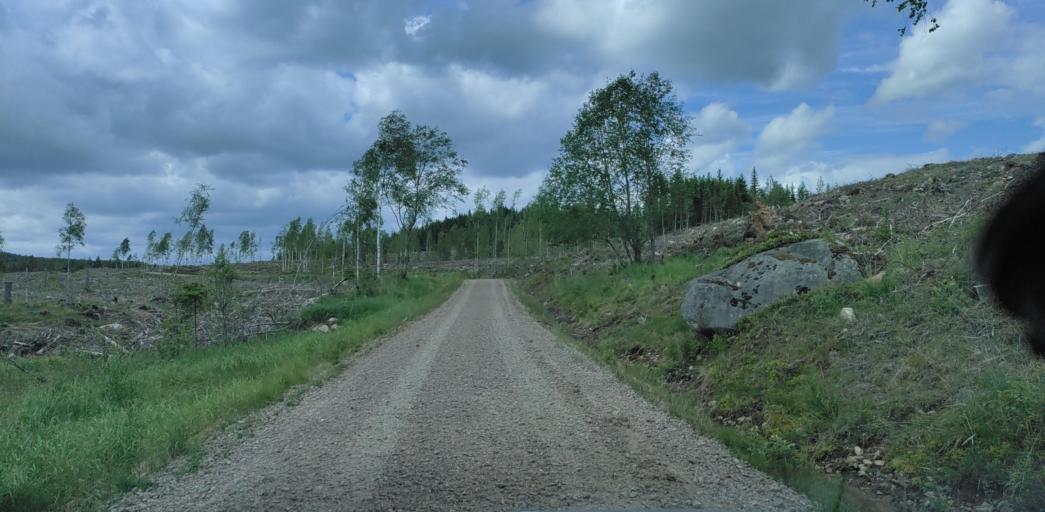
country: SE
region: Vaermland
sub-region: Munkfors Kommun
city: Munkfors
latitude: 59.9482
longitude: 13.4192
